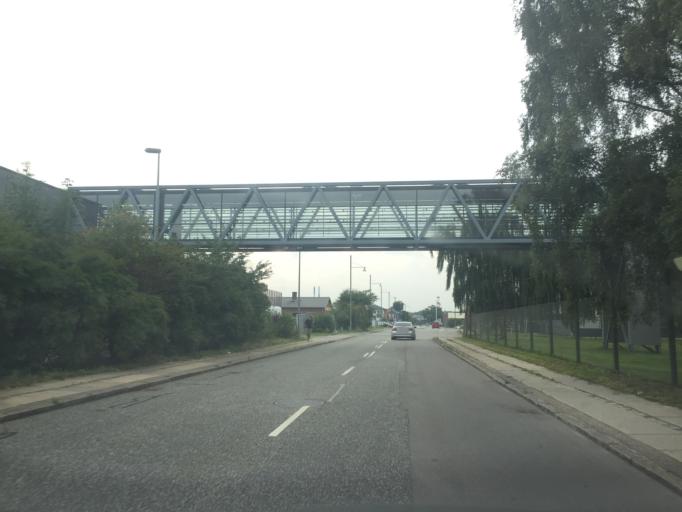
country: DK
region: Capital Region
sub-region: Albertslund Kommune
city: Albertslund
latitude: 55.6615
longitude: 12.3765
